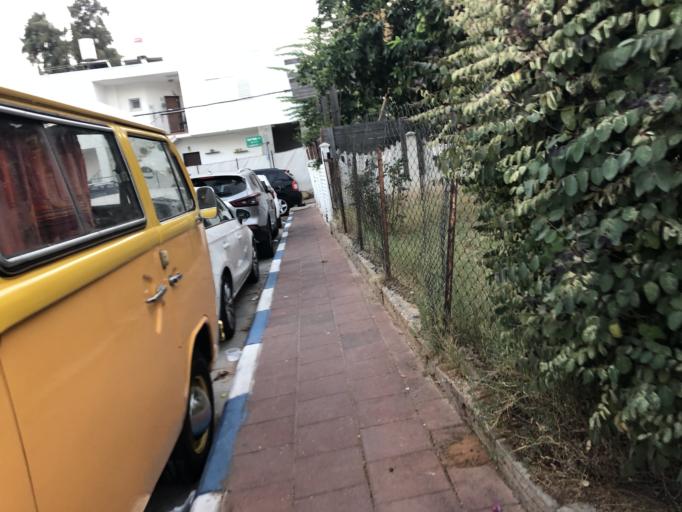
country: IL
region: Tel Aviv
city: Giv`atayim
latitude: 32.0684
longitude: 34.8176
